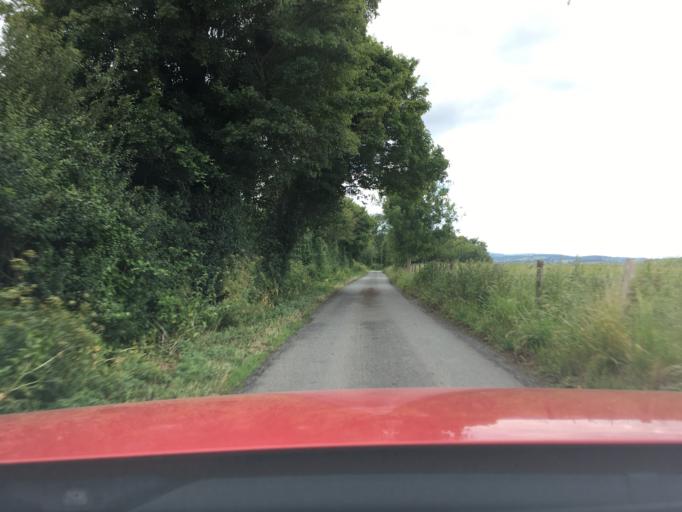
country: GB
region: England
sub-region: Gloucestershire
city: Stonehouse
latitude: 51.7938
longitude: -2.3790
